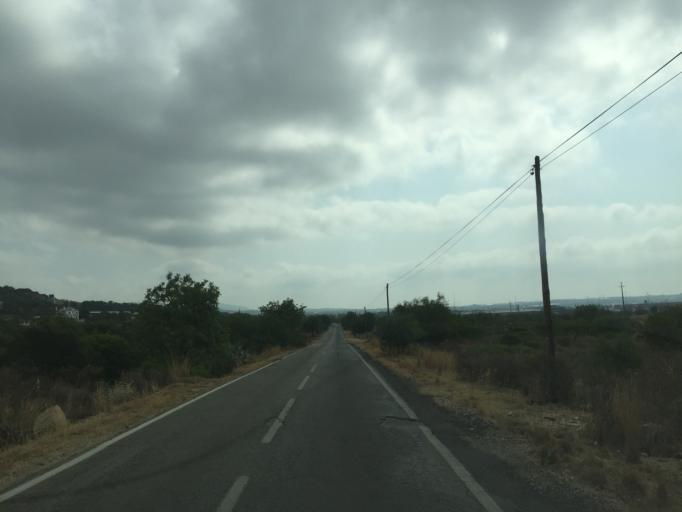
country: PT
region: Faro
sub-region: Faro
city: Santa Barbara de Nexe
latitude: 37.0910
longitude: -7.9359
